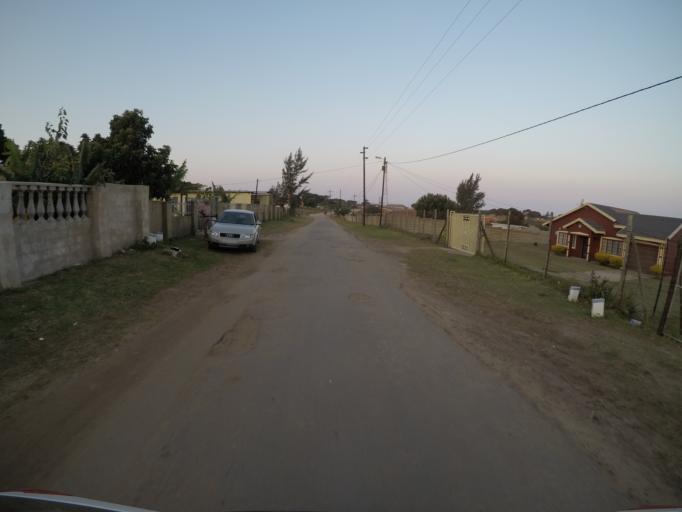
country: ZA
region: KwaZulu-Natal
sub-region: uThungulu District Municipality
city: Richards Bay
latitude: -28.7611
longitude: 32.1281
